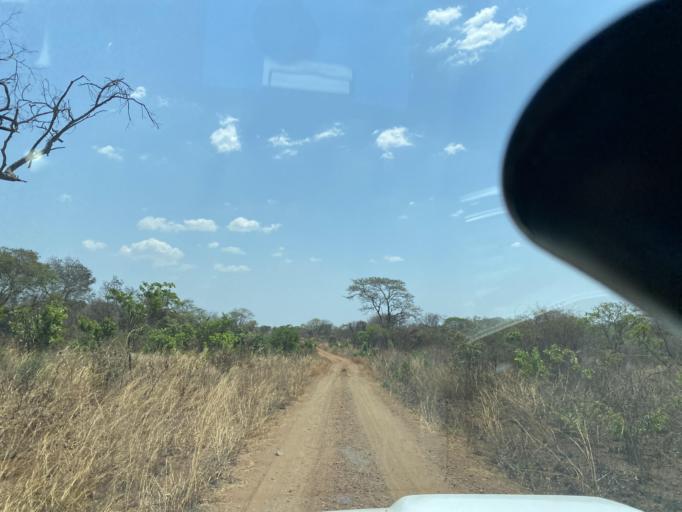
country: ZM
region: Lusaka
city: Lusaka
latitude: -15.5085
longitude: 28.0032
